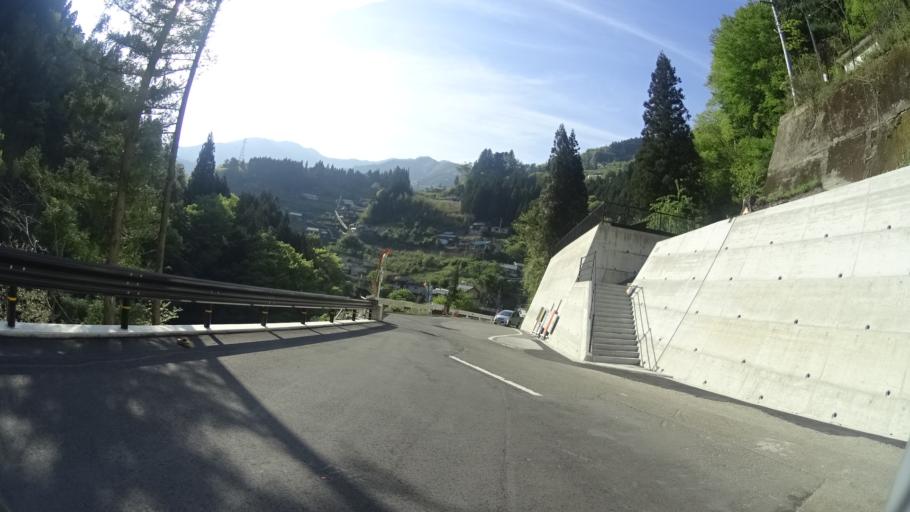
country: JP
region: Tokushima
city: Ikedacho
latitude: 33.8789
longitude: 133.9376
